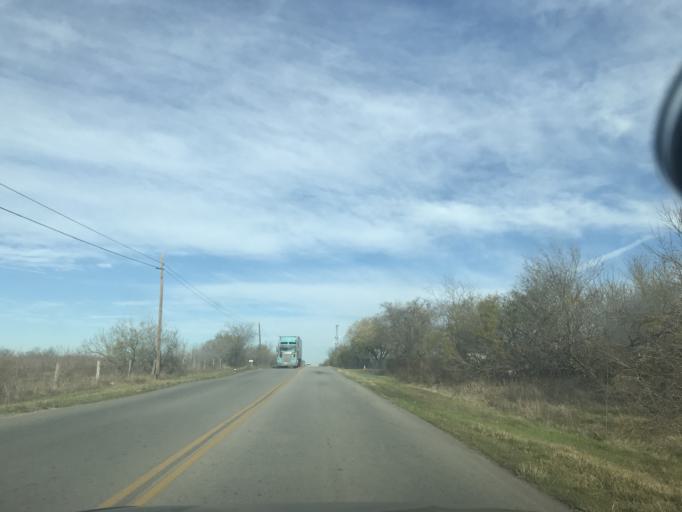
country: US
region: Texas
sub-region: Travis County
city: Manor
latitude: 30.3253
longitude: -97.5447
